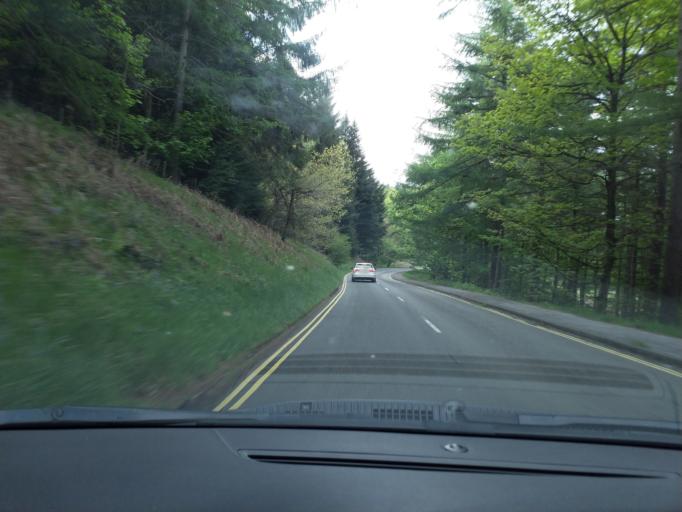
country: GB
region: England
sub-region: Derbyshire
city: Hope Valley
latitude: 53.3833
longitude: -1.7192
